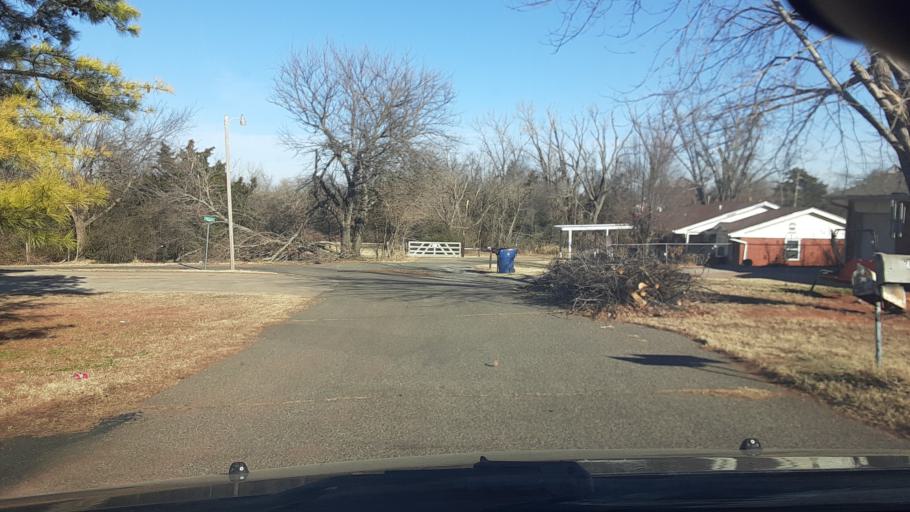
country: US
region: Oklahoma
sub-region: Logan County
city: Guthrie
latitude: 35.8580
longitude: -97.4311
